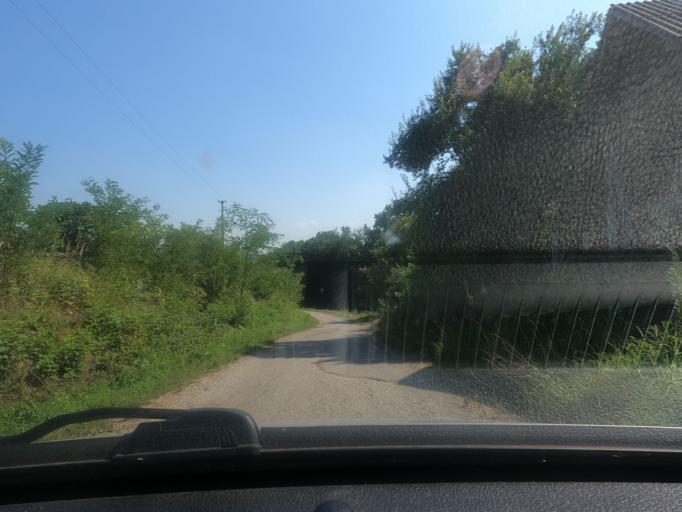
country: RS
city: Jarebice
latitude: 44.5420
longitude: 19.3761
